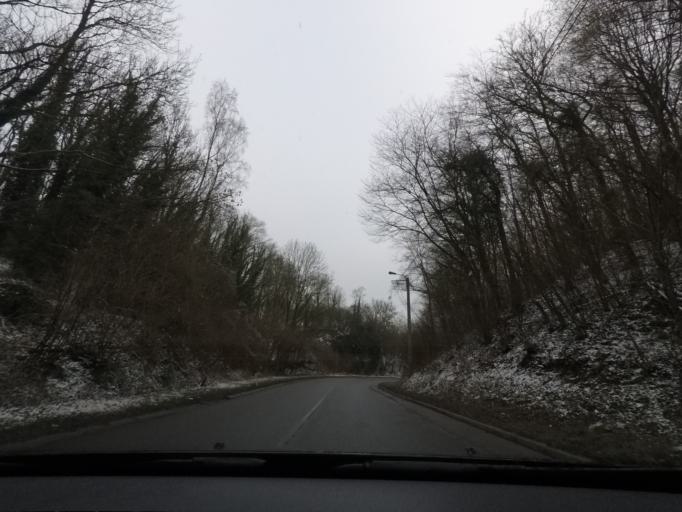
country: BE
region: Wallonia
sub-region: Province de Namur
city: Gembloux
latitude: 50.4881
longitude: 4.6864
